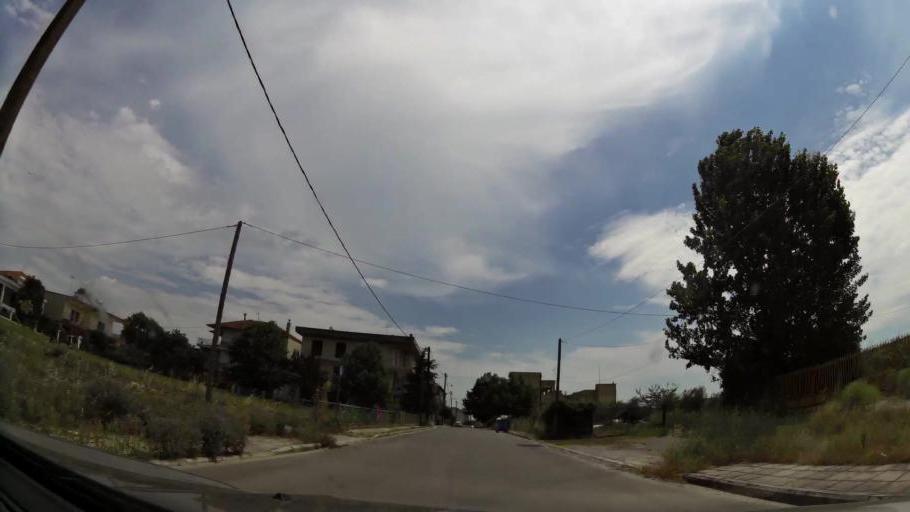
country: GR
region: Central Macedonia
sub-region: Nomos Pierias
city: Katerini
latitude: 40.2590
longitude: 22.5065
